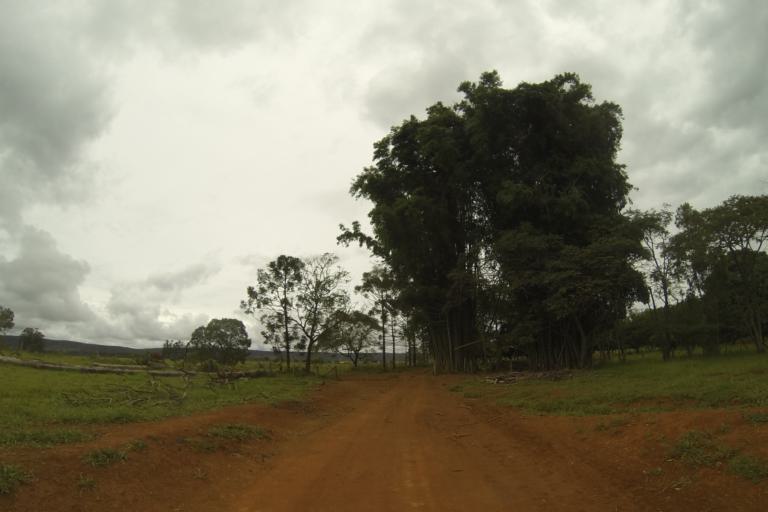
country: BR
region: Minas Gerais
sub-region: Ibia
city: Ibia
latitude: -19.7339
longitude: -46.6070
